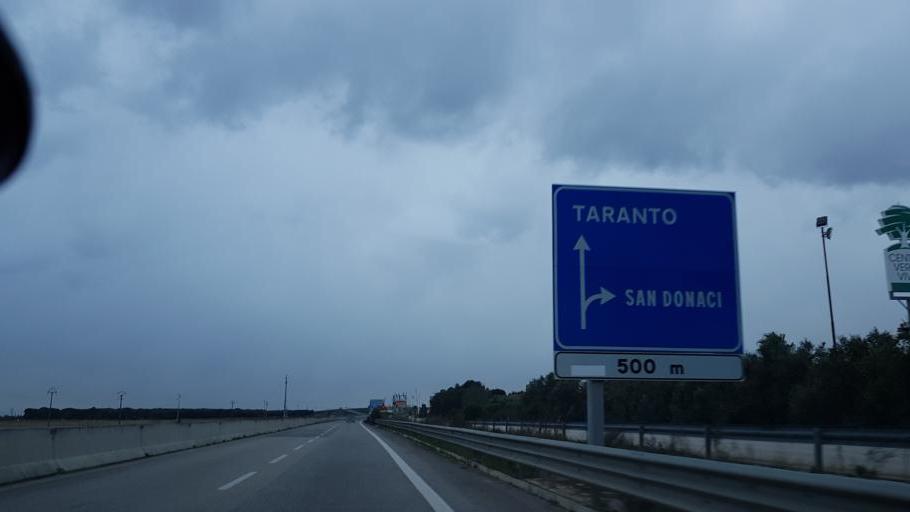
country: IT
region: Apulia
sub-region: Provincia di Brindisi
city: Mesagne
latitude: 40.5959
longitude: 17.8680
